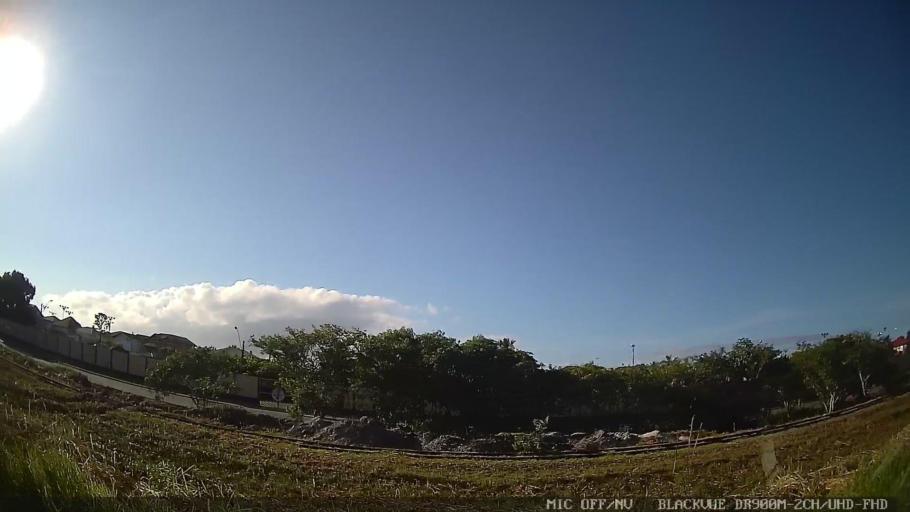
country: BR
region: Sao Paulo
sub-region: Peruibe
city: Peruibe
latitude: -24.2798
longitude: -46.9586
